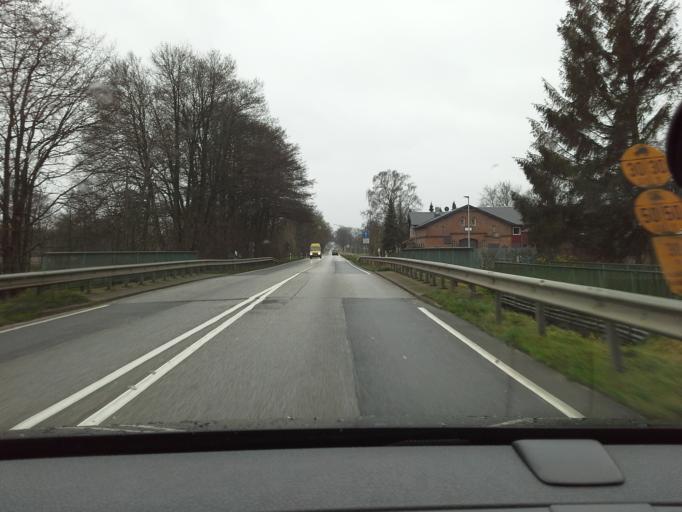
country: DE
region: Schleswig-Holstein
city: Bilsen
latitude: 53.7476
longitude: 9.8861
